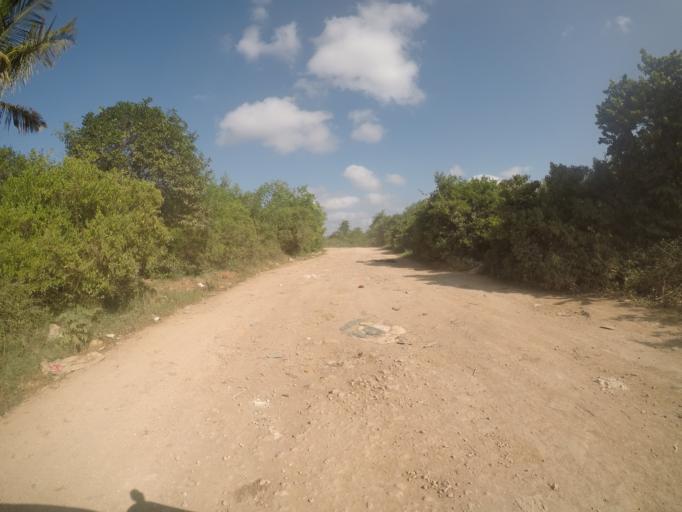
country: TZ
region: Zanzibar Central/South
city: Koani
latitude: -6.2189
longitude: 39.3267
